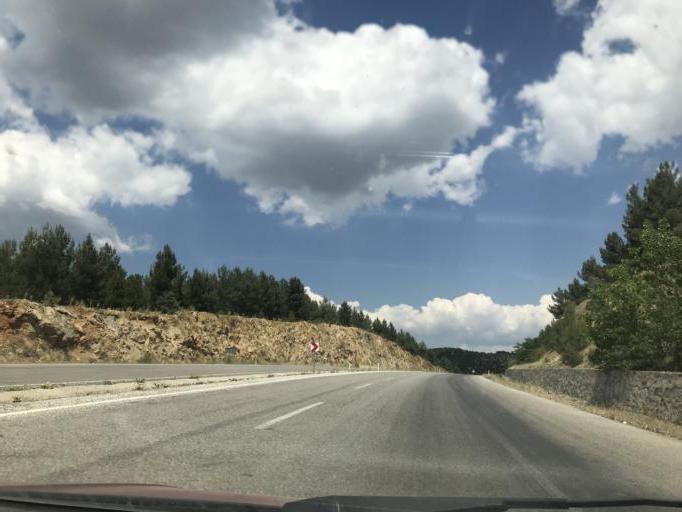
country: TR
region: Denizli
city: Tavas
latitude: 37.5810
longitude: 29.0924
